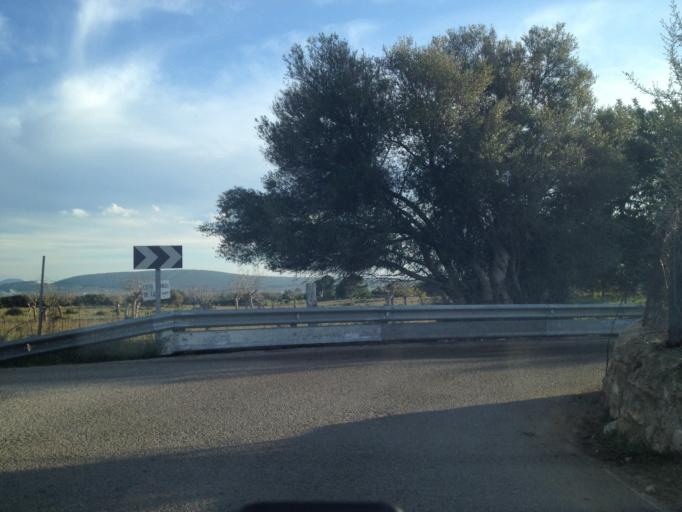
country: ES
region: Balearic Islands
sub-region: Illes Balears
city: Consell
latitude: 39.6743
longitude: 2.7888
